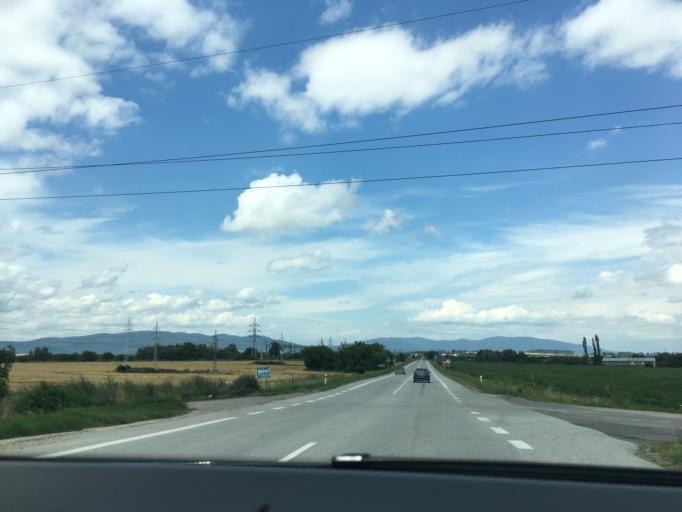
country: SK
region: Kosicky
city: Trebisov
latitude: 48.6273
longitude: 21.6960
